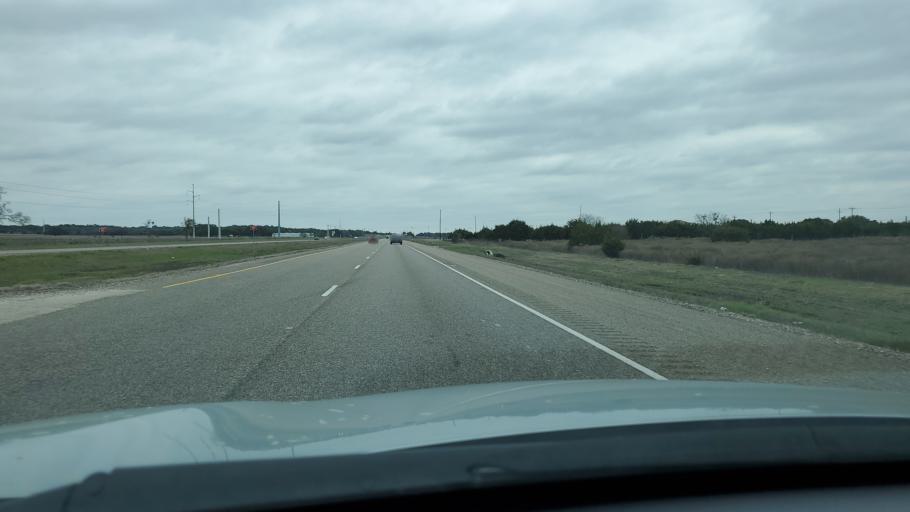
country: US
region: Texas
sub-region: Williamson County
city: Florence
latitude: 30.7798
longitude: -97.7612
